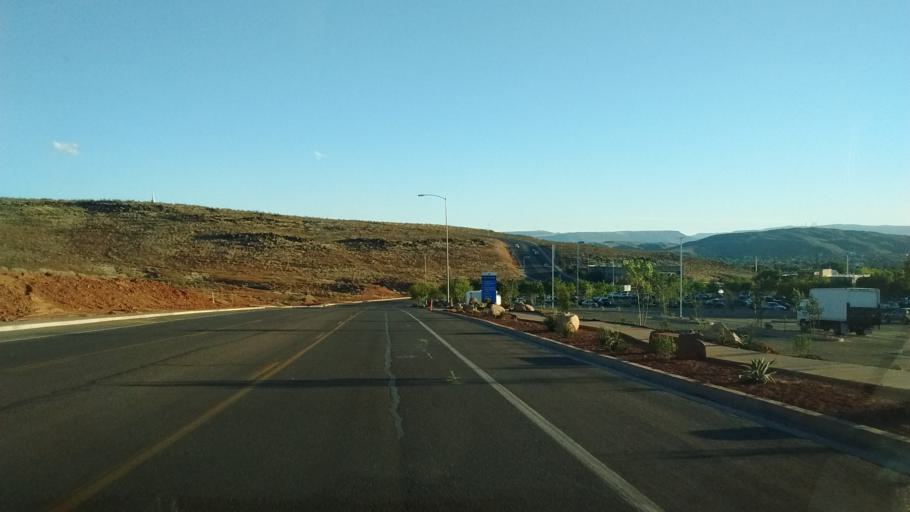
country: US
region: Utah
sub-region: Washington County
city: Saint George
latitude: 37.0984
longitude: -113.5494
